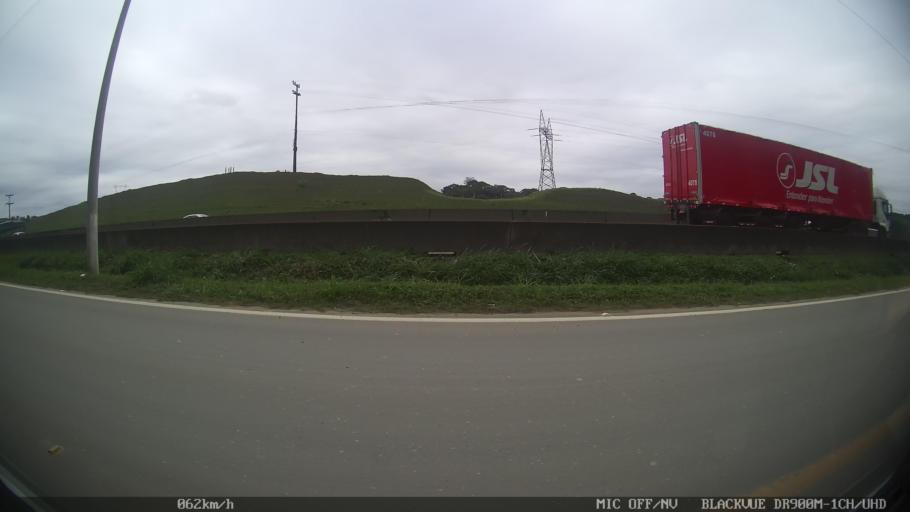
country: BR
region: Santa Catarina
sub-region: Joinville
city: Joinville
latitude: -26.2772
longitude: -48.8929
